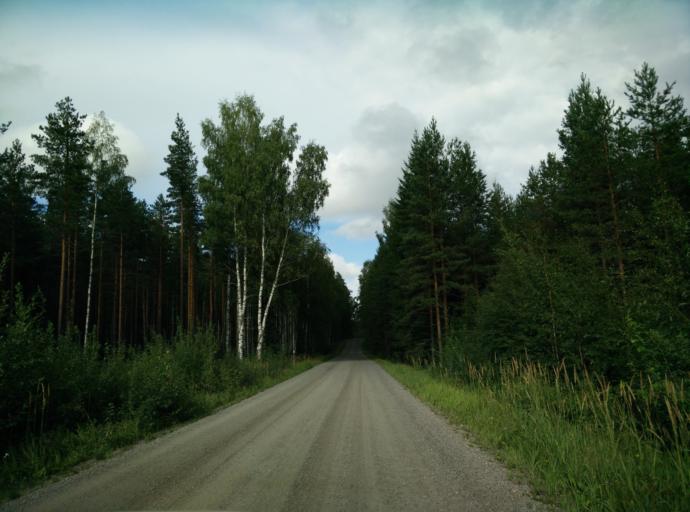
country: FI
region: Haeme
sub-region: Haemeenlinna
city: Kalvola
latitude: 61.1096
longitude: 24.1299
